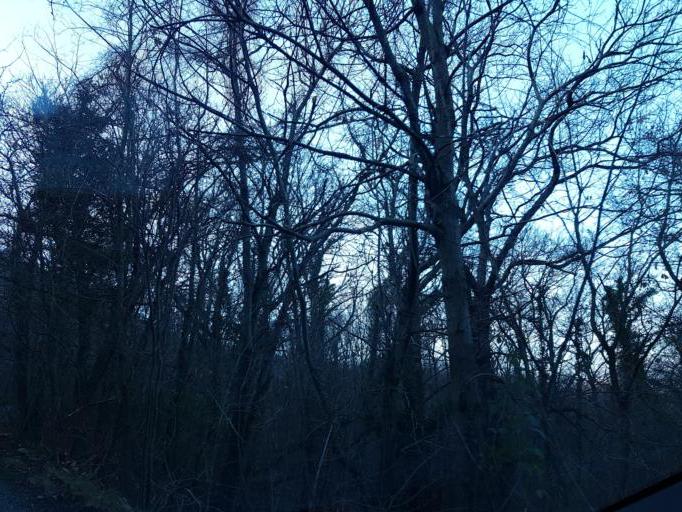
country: IT
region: Liguria
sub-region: Provincia di Genova
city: Manesseno
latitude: 44.4614
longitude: 8.9313
